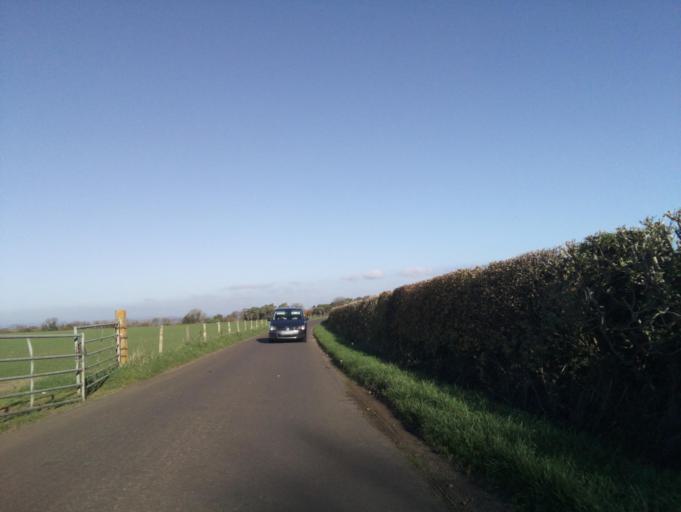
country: GB
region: England
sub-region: Somerset
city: Milborne Port
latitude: 51.0181
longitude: -2.5039
